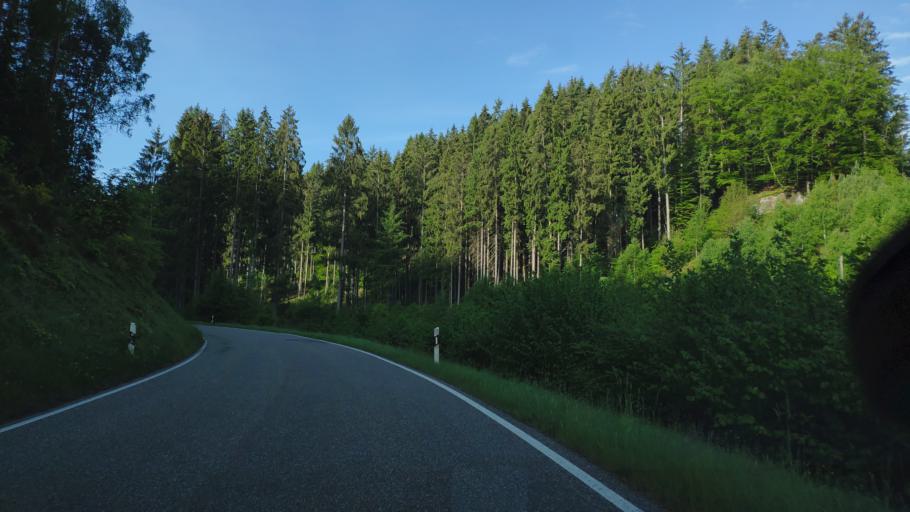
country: DE
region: Rheinland-Pfalz
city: Ruppertsweiler
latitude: 49.1621
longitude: 7.7131
